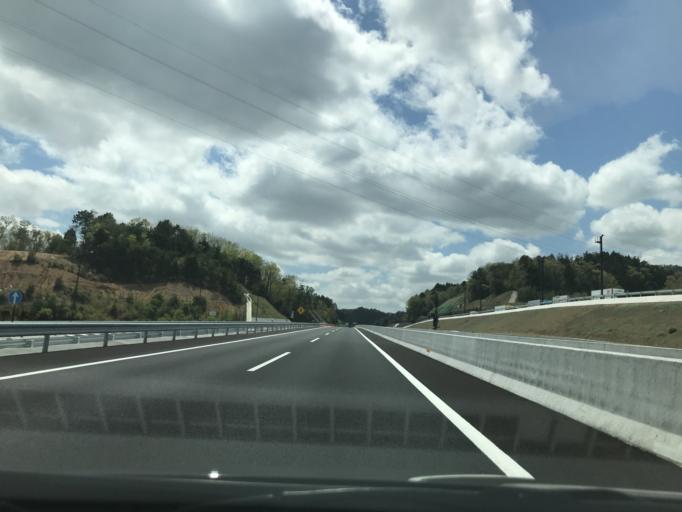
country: JP
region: Osaka
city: Ibaraki
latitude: 34.8809
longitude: 135.5306
